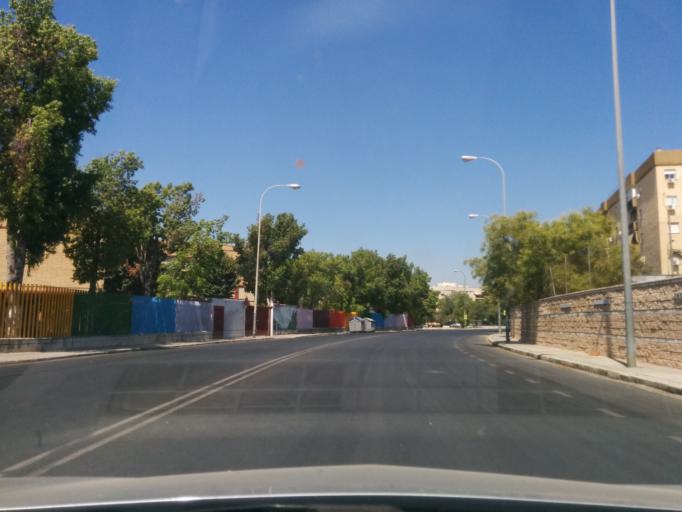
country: ES
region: Andalusia
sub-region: Provincia de Sevilla
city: Sevilla
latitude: 37.3625
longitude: -5.9718
